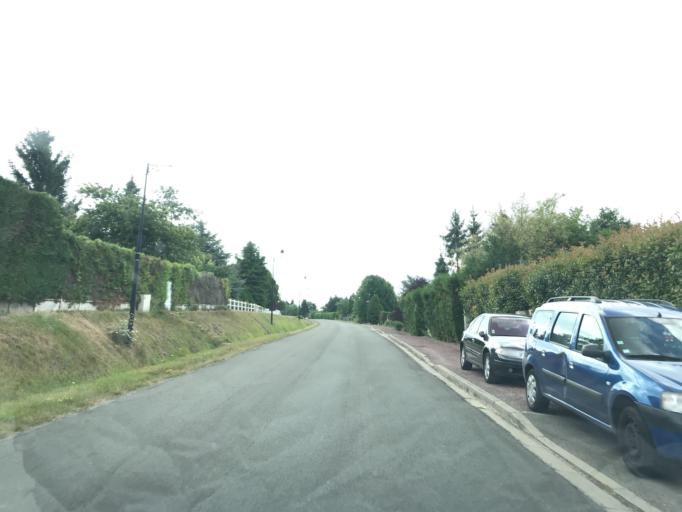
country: FR
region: Haute-Normandie
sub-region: Departement de l'Eure
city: Houlbec-Cocherel
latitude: 49.0710
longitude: 1.3118
